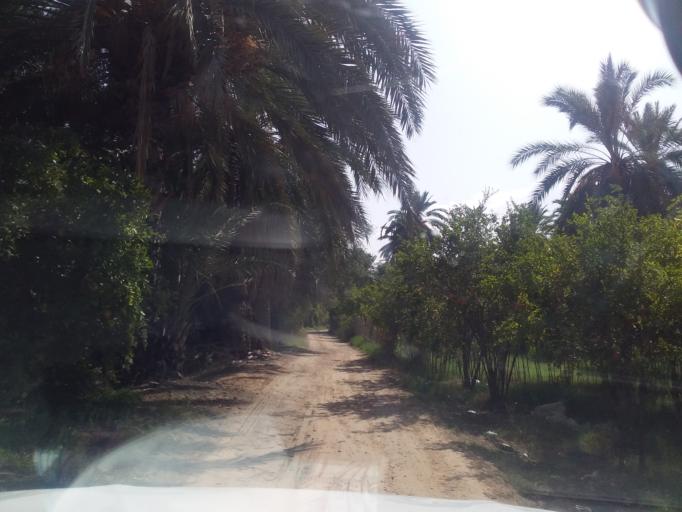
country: TN
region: Qabis
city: Gabes
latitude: 33.6258
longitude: 10.2878
